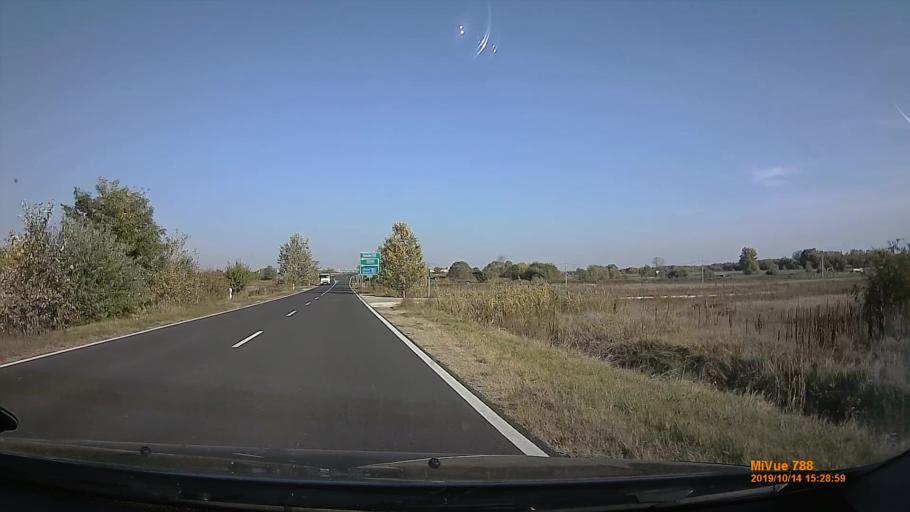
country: HU
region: Pest
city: Ecser
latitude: 47.4315
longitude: 19.3197
